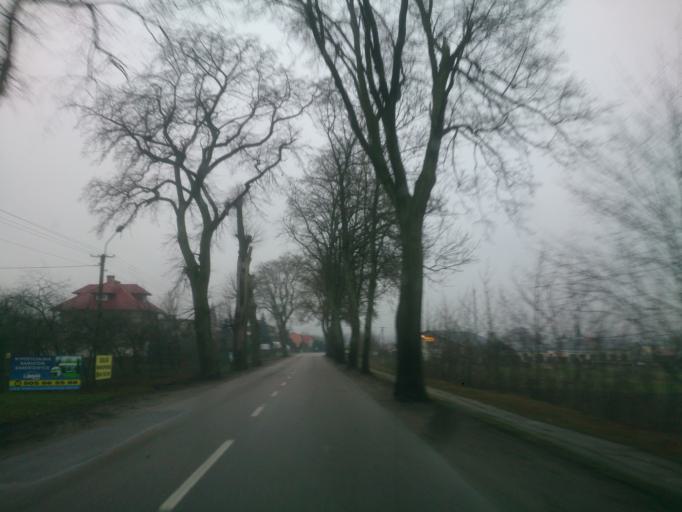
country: PL
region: Pomeranian Voivodeship
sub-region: Powiat koscierski
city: Stara Kiszewa
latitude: 53.9918
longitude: 18.1772
